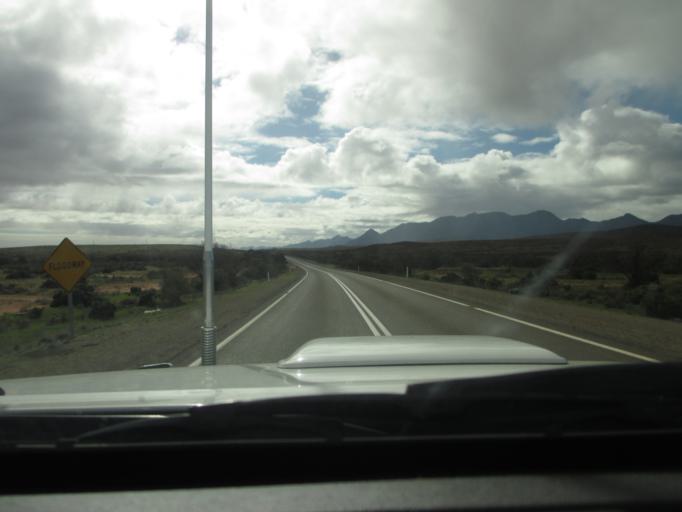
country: AU
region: South Australia
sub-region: Flinders Ranges
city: Quorn
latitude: -31.5905
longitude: 138.4134
